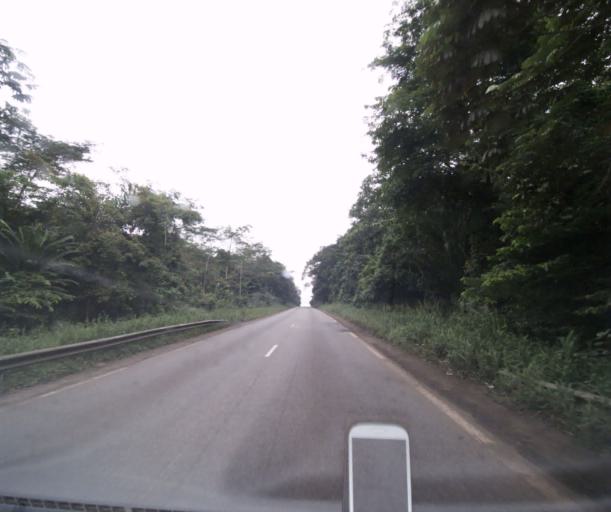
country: CM
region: Littoral
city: Edea
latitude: 3.8079
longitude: 10.2719
